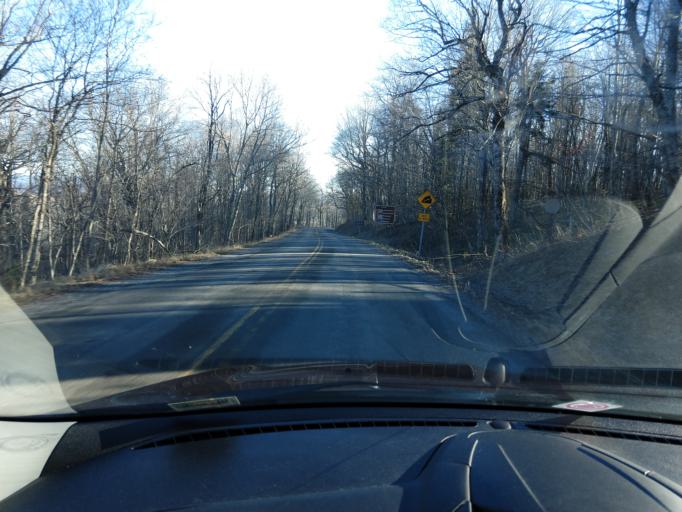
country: US
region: Virginia
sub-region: Highland County
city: Monterey
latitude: 38.4703
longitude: -79.6959
